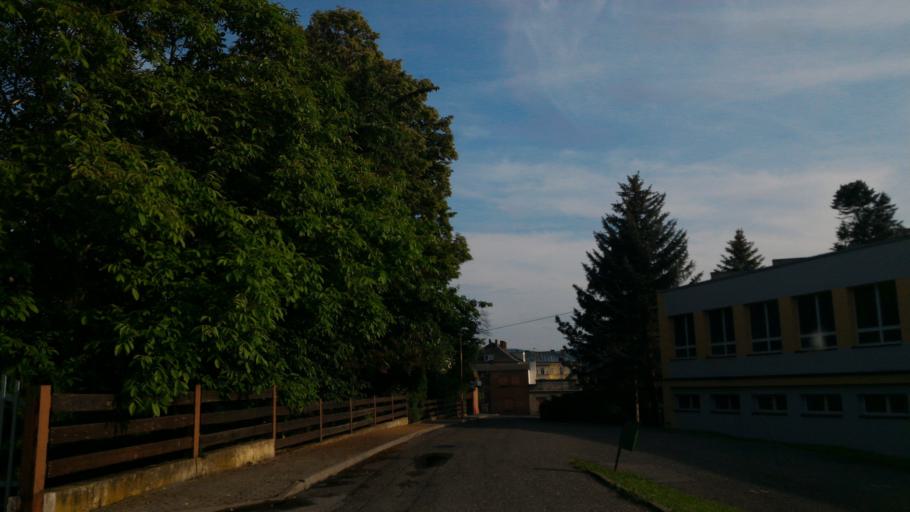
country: CZ
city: Hradek nad Nisou
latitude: 50.8568
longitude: 14.8437
